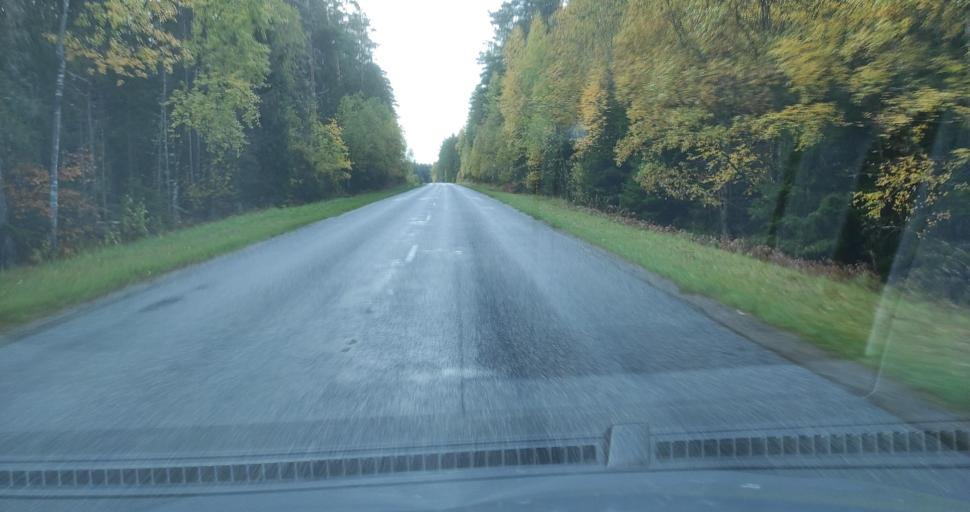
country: LV
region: Skrunda
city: Skrunda
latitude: 56.6417
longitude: 22.0084
